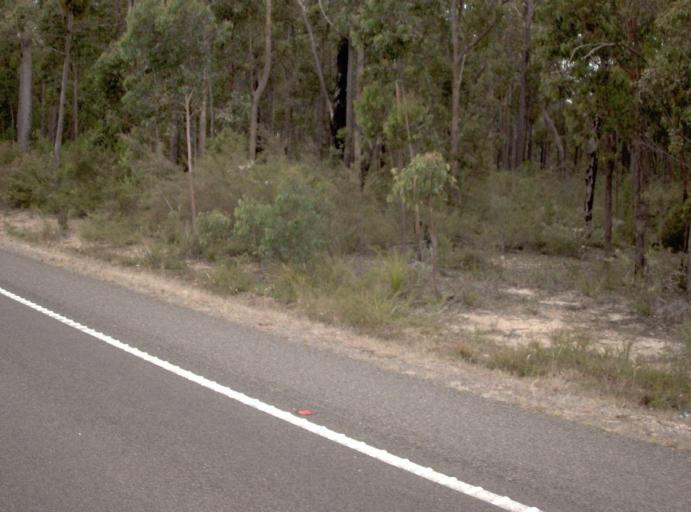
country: AU
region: Victoria
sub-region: East Gippsland
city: Lakes Entrance
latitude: -37.7221
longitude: 147.9559
